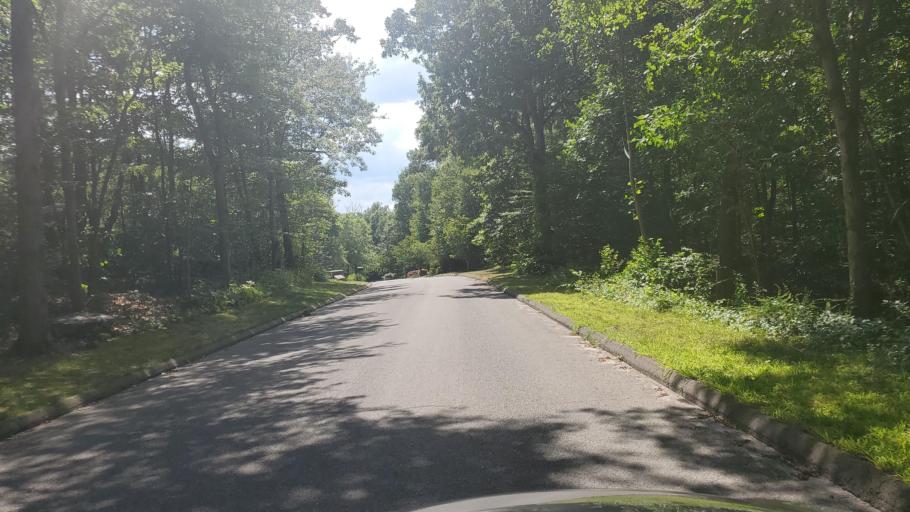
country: US
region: Connecticut
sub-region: Fairfield County
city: Newtown
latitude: 41.3514
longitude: -73.2768
